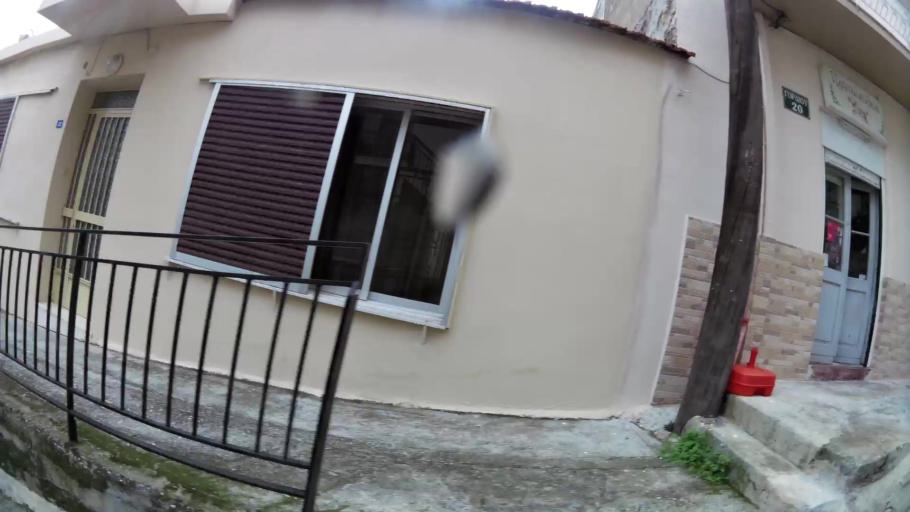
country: GR
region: Attica
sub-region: Nomos Piraios
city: Nikaia
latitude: 37.9606
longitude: 23.6449
